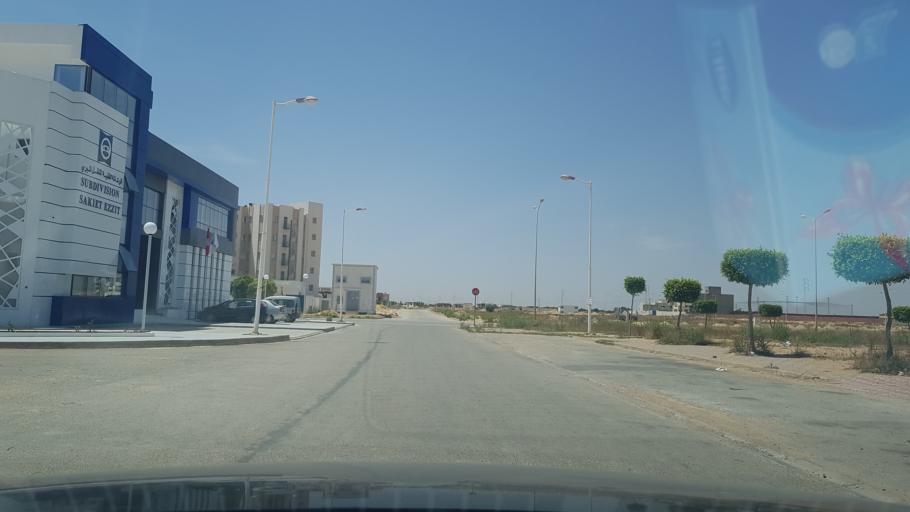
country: TN
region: Safaqis
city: Al Qarmadah
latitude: 34.8418
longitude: 10.7573
